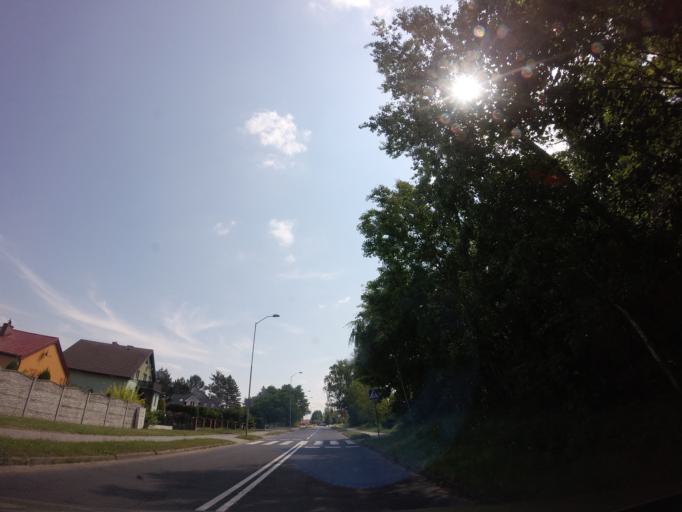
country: PL
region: West Pomeranian Voivodeship
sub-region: Powiat gryfinski
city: Stare Czarnowo
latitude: 53.3517
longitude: 14.7426
